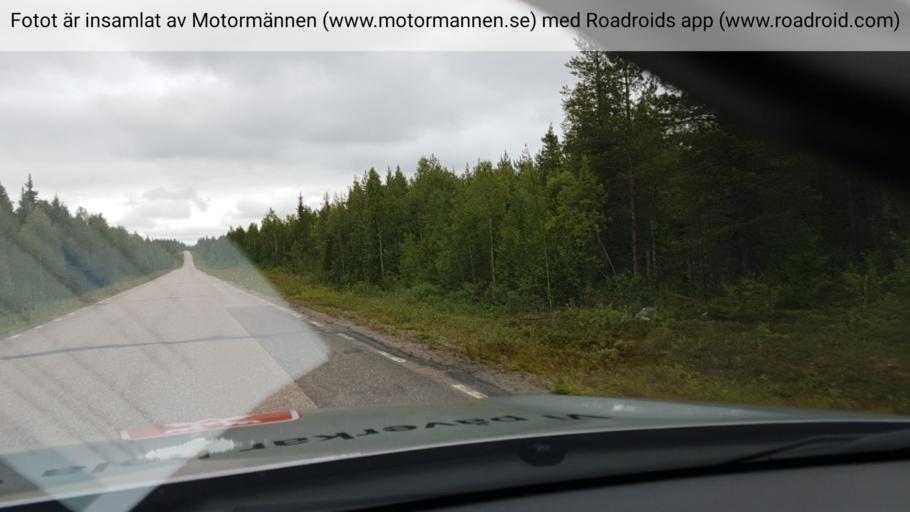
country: SE
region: Norrbotten
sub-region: Overkalix Kommun
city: OEverkalix
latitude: 67.0355
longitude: 22.0259
